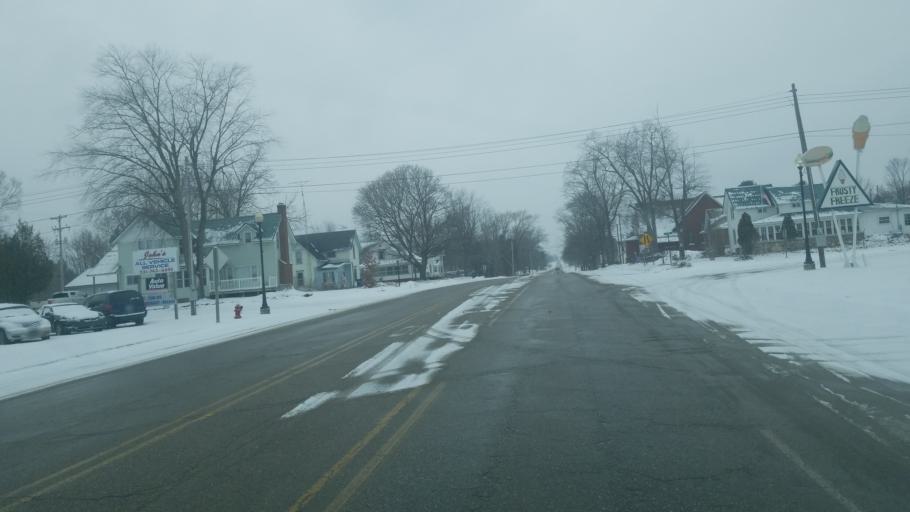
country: US
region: Michigan
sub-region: Osceola County
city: Evart
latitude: 44.1025
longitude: -85.1481
